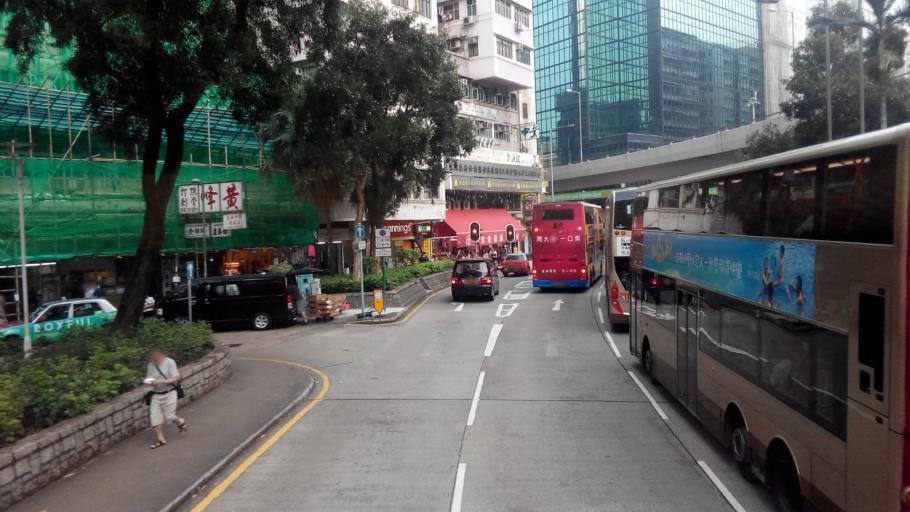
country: HK
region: Sham Shui Po
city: Sham Shui Po
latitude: 22.3268
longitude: 114.1673
